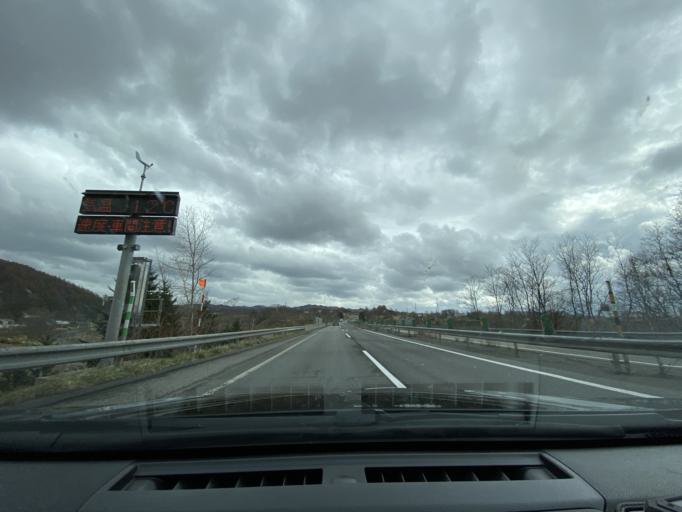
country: JP
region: Hokkaido
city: Sunagawa
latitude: 43.5052
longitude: 141.9301
